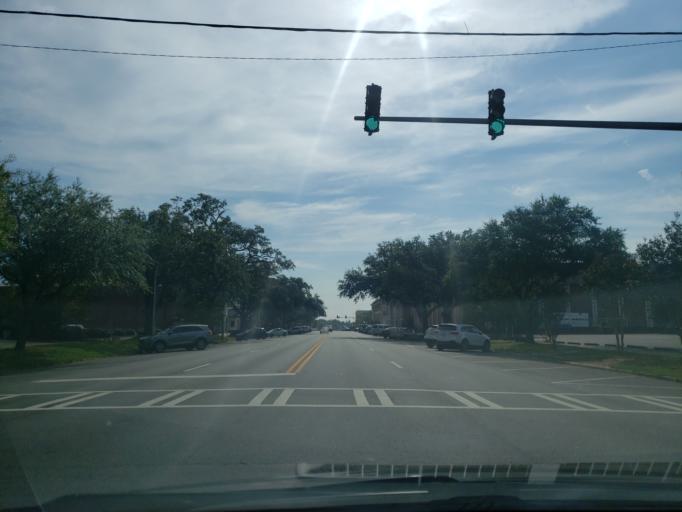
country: US
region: Georgia
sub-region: Dougherty County
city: Albany
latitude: 31.5784
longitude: -84.1560
